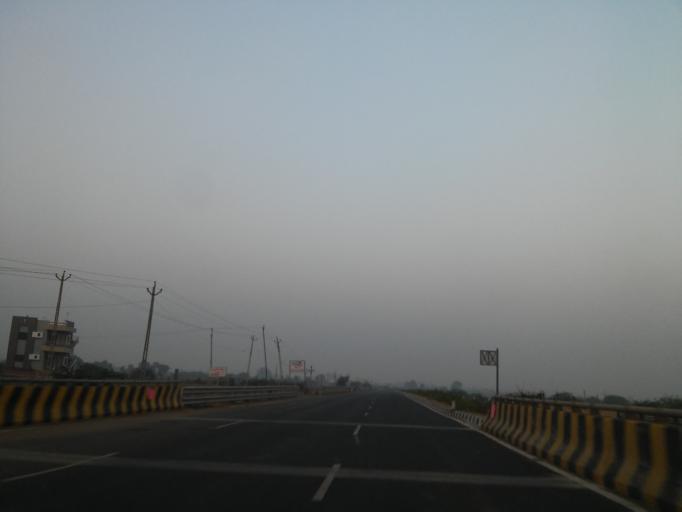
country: IN
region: Gujarat
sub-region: Surendranagar
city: Dhrangadhra
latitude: 23.0005
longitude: 71.3631
